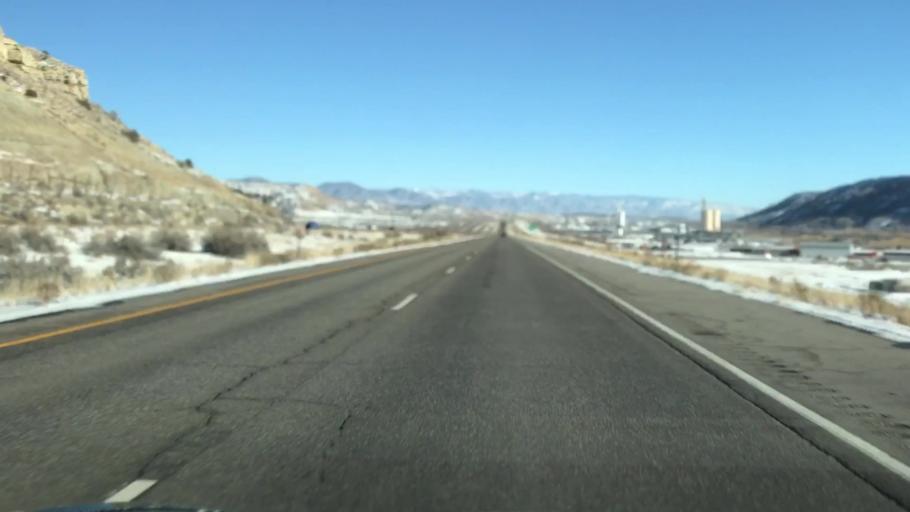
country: US
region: Colorado
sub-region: Garfield County
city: Rifle
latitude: 39.5123
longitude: -107.8702
